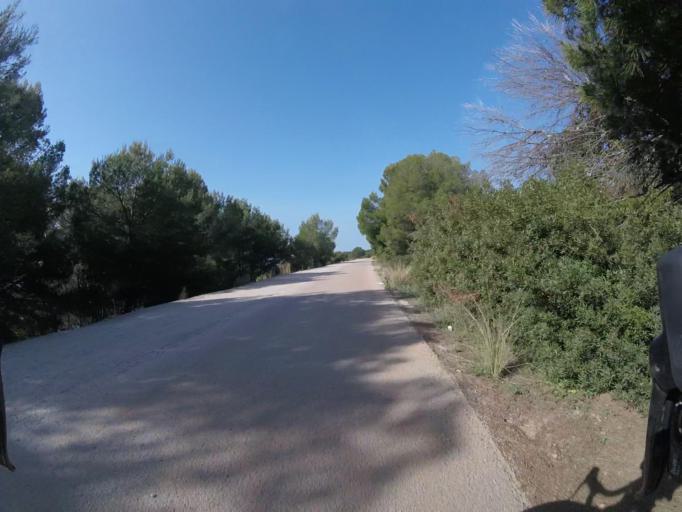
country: ES
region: Valencia
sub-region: Provincia de Castello
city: Orpesa/Oropesa del Mar
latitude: 40.0661
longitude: 0.1240
